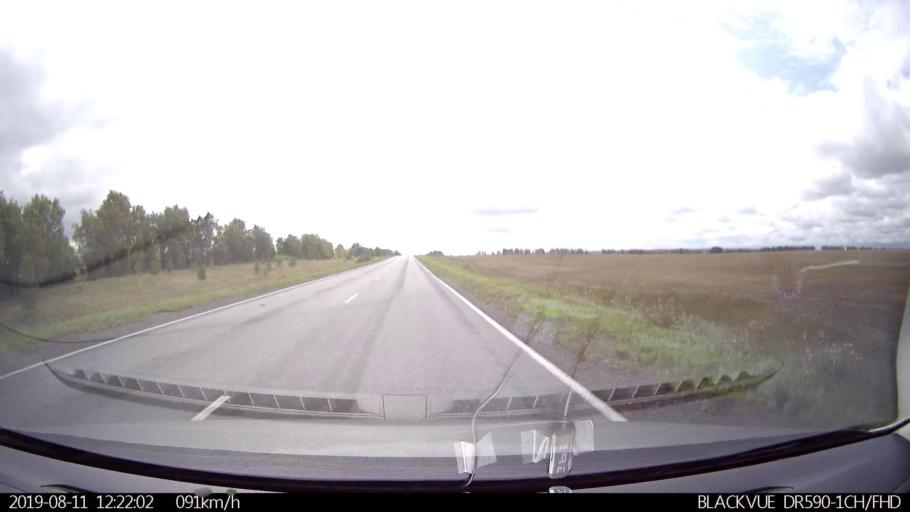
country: RU
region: Ulyanovsk
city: Ignatovka
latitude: 53.9139
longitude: 47.9559
